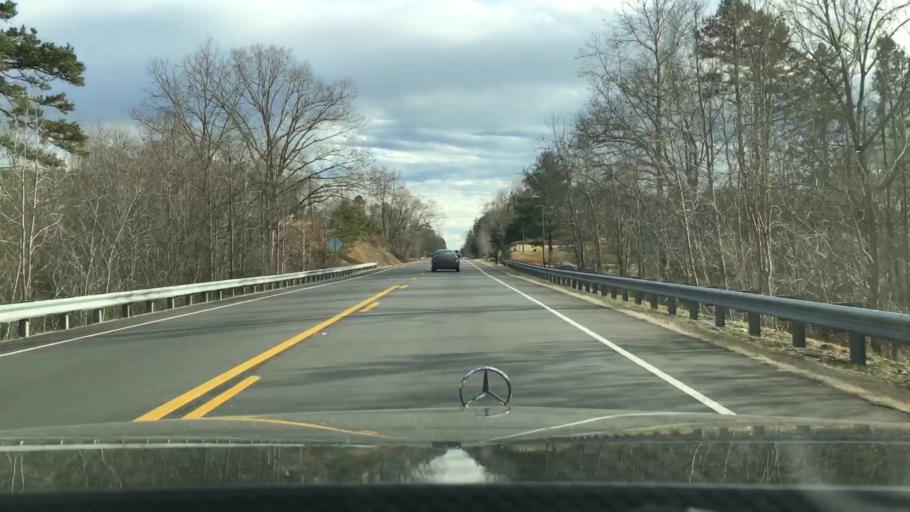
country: US
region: North Carolina
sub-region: Caswell County
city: Yanceyville
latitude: 36.4572
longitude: -79.3705
